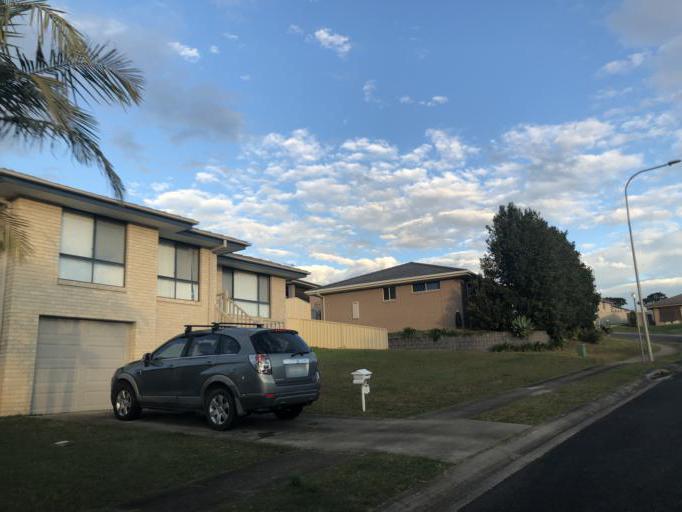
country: AU
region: New South Wales
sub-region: Nambucca Shire
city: Macksville
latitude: -30.7313
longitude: 152.9089
